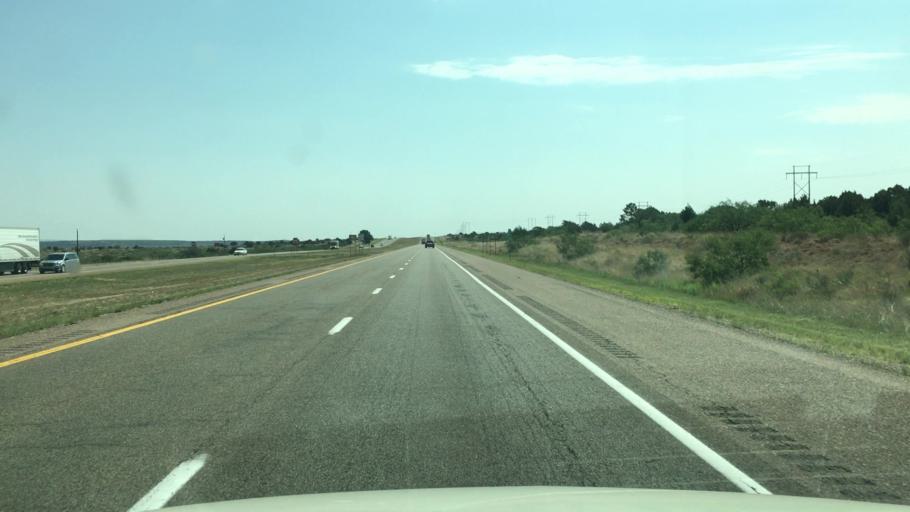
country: US
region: New Mexico
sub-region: Guadalupe County
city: Santa Rosa
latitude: 35.0477
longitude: -104.3735
